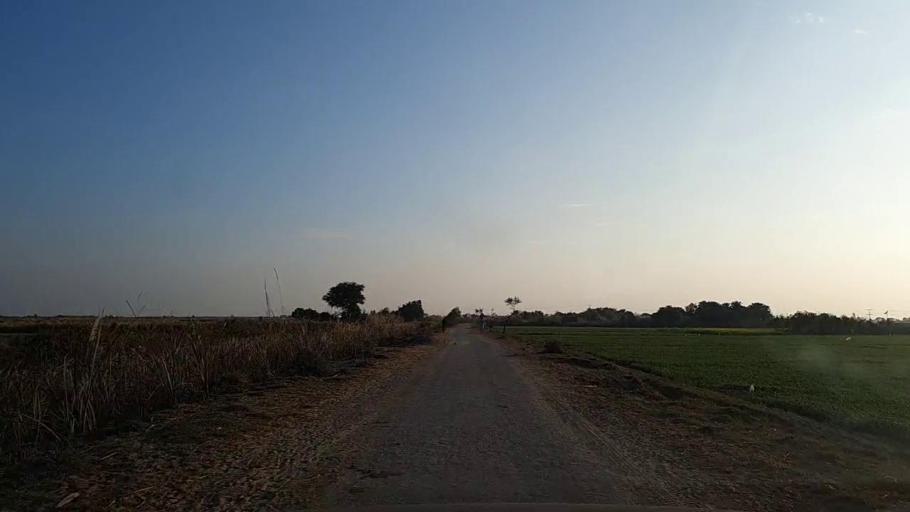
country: PK
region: Sindh
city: Sanghar
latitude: 26.2737
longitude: 68.9825
